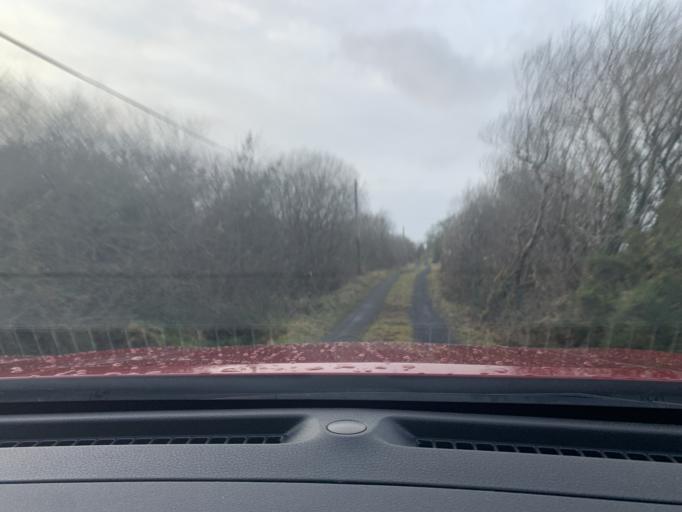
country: IE
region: Connaught
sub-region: Roscommon
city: Ballaghaderreen
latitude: 53.9523
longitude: -8.5360
